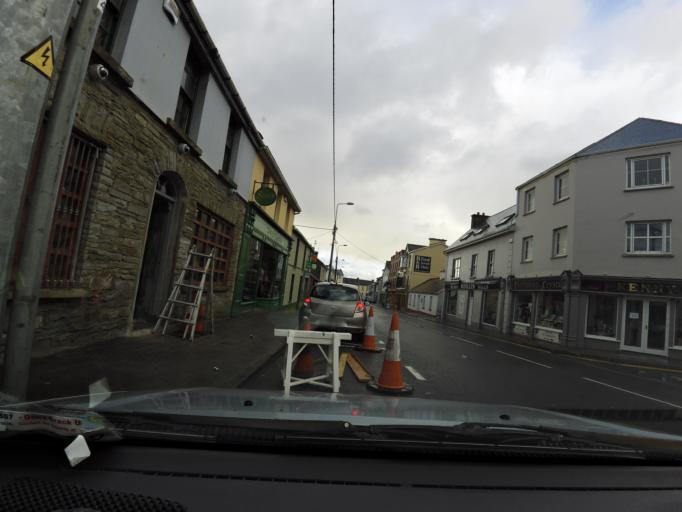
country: IE
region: Munster
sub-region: An Clar
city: Kilrush
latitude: 52.9317
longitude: -9.3458
